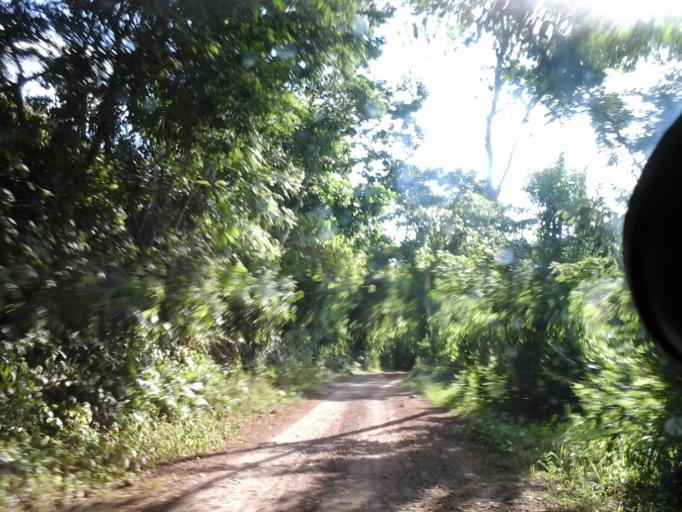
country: CO
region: Cesar
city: San Diego
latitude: 10.2459
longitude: -73.1253
